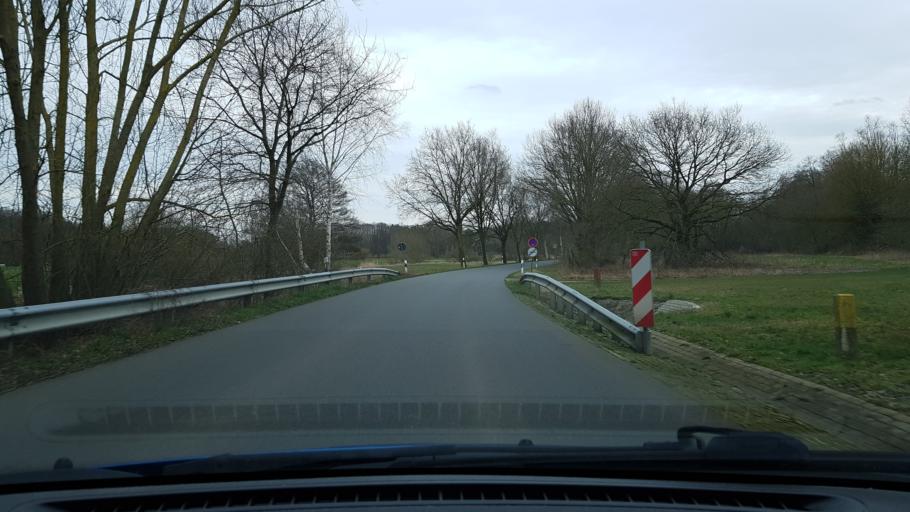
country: DE
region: Lower Saxony
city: Bad Bevensen
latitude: 53.0557
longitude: 10.5994
